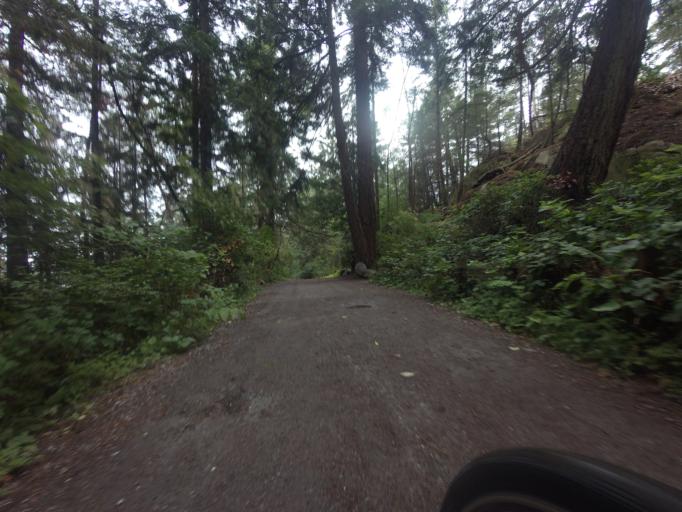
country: CA
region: British Columbia
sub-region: Greater Vancouver Regional District
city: Bowen Island
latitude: 49.3340
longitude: -123.2633
